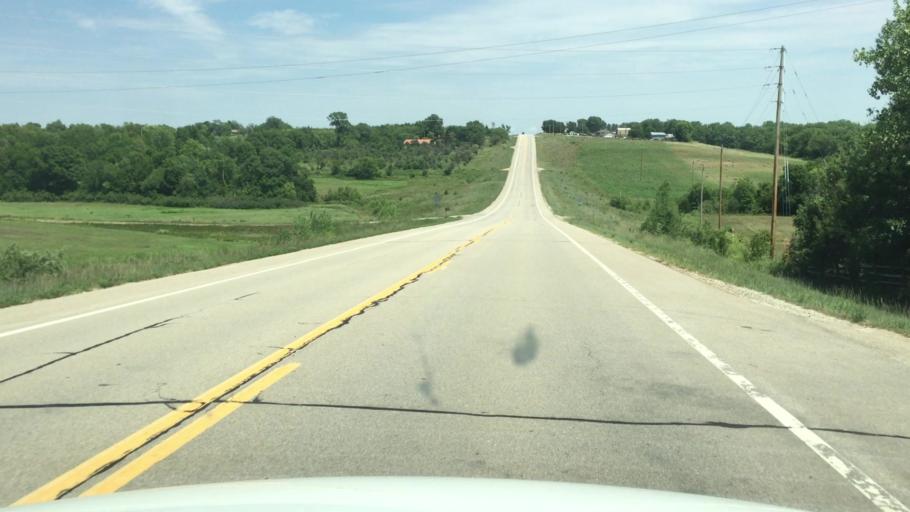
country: US
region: Kansas
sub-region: Douglas County
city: Lawrence
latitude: 38.9712
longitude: -95.4357
